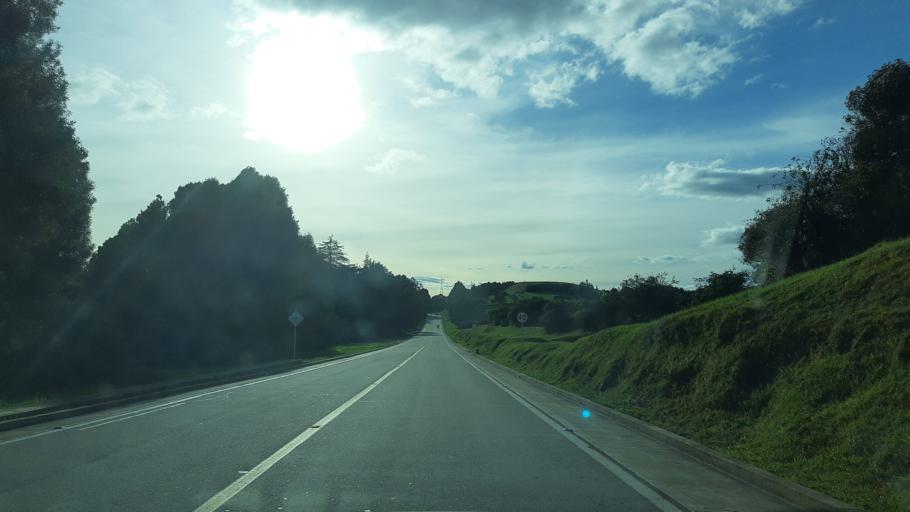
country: CO
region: Cundinamarca
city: Choconta
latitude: 5.0951
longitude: -73.7057
